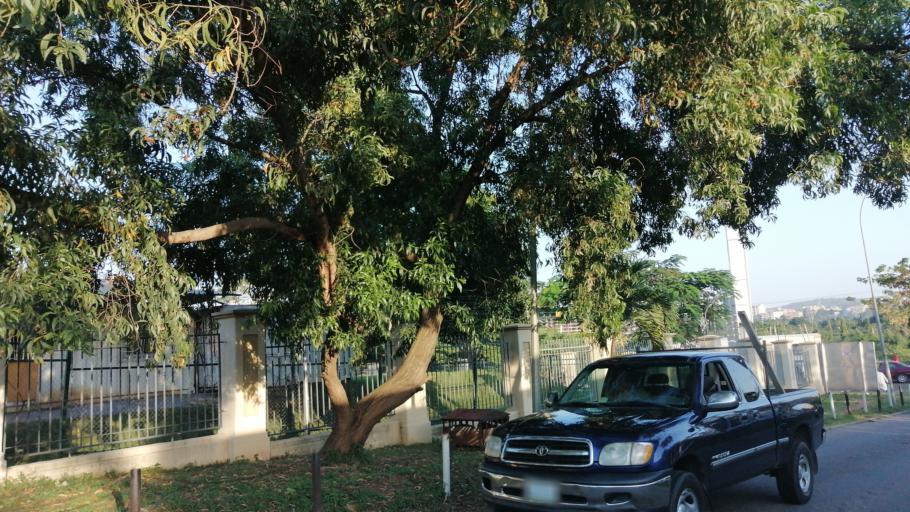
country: NG
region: Abuja Federal Capital Territory
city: Abuja
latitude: 9.0649
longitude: 7.4869
